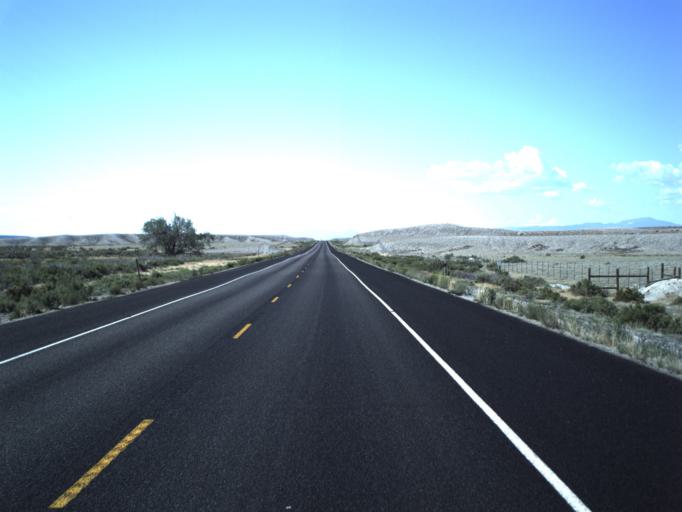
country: US
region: Utah
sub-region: Emery County
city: Ferron
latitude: 38.9917
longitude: -111.1679
